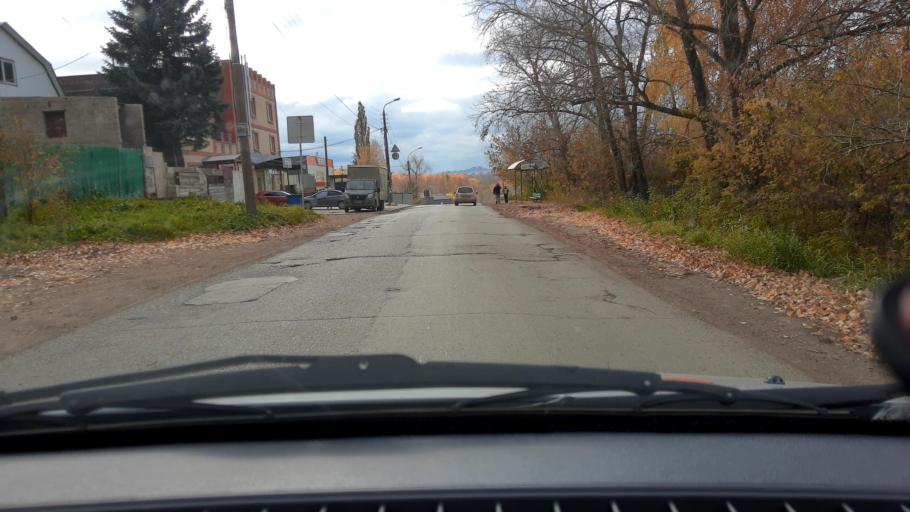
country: RU
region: Bashkortostan
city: Ufa
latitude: 54.8356
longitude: 56.1436
